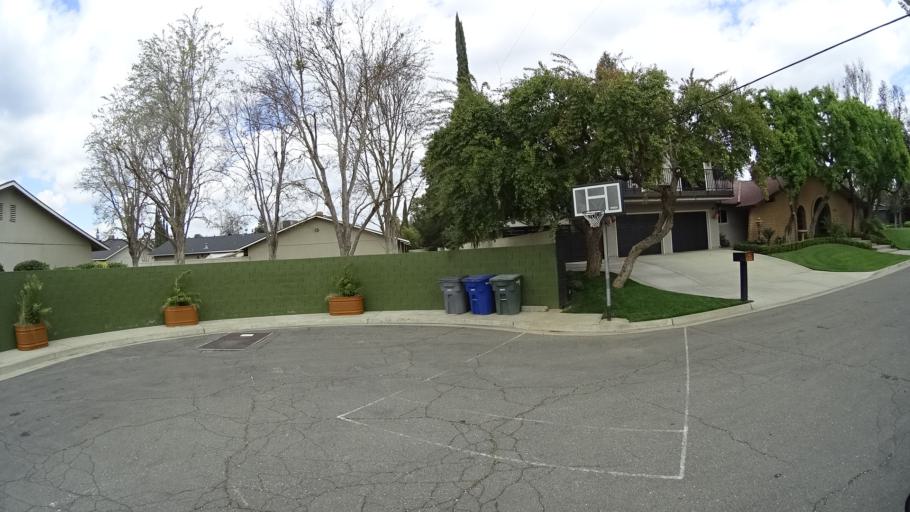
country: US
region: California
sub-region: Fresno County
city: Fresno
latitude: 36.8237
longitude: -119.8423
